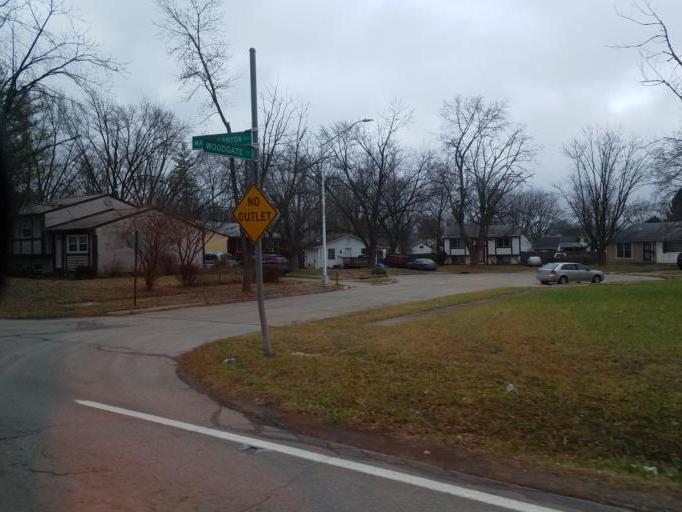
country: US
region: Ohio
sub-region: Franklin County
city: Minerva Park
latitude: 40.0910
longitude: -82.9599
